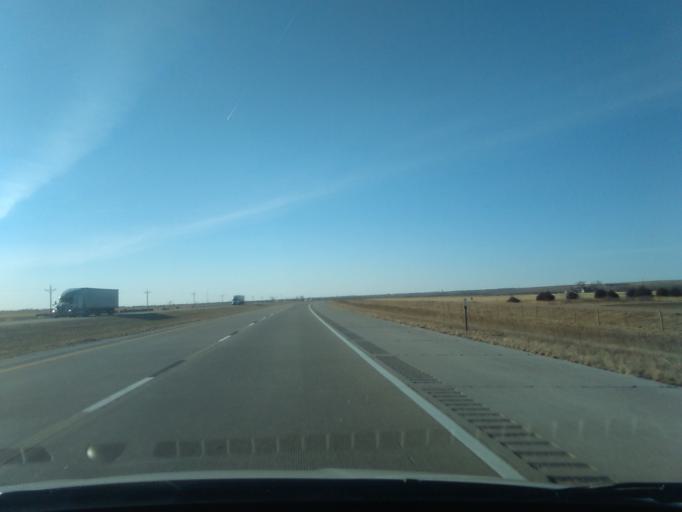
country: US
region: Colorado
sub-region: Sedgwick County
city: Julesburg
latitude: 41.0627
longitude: -101.9961
